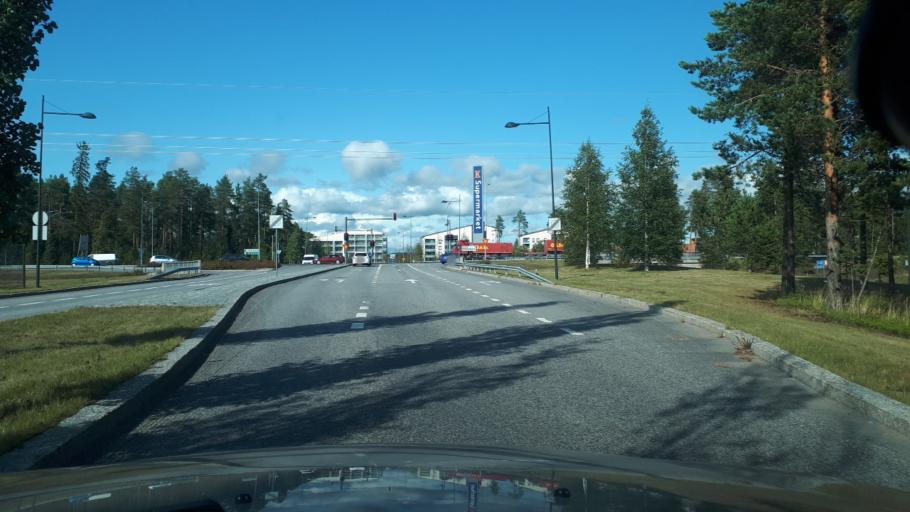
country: FI
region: Northern Ostrobothnia
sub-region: Oulu
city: Oulu
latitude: 65.0776
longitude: 25.4517
